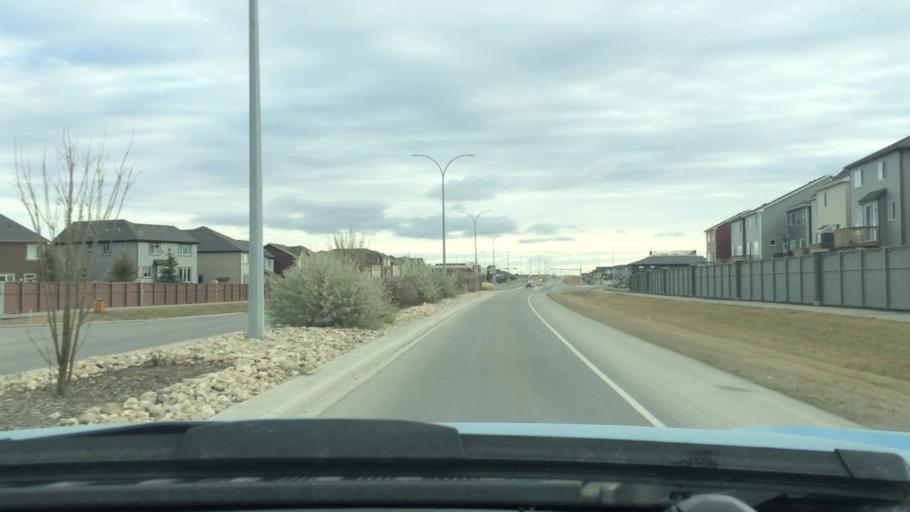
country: CA
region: Alberta
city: Airdrie
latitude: 51.2561
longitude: -114.0300
